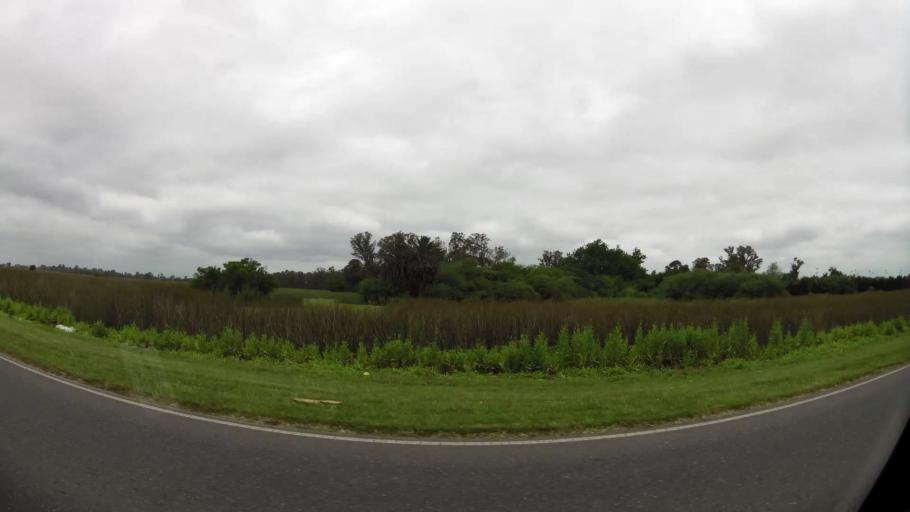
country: AR
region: Buenos Aires
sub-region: Partido de San Vicente
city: San Vicente
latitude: -34.9920
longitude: -58.4690
